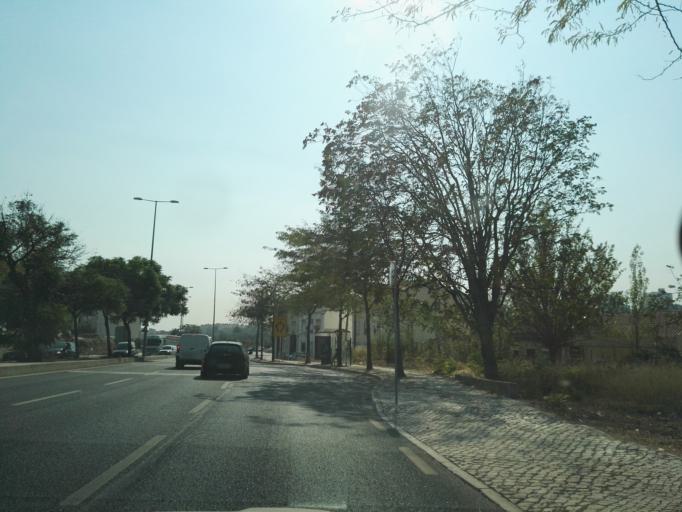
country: PT
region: Lisbon
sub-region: Loures
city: Moscavide
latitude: 38.7513
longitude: -9.1044
